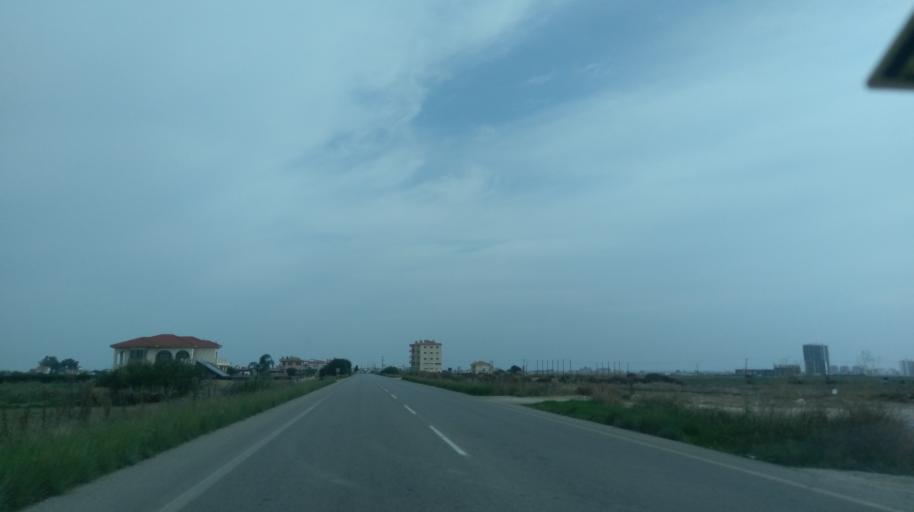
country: CY
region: Ammochostos
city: Trikomo
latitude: 35.2794
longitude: 33.8867
